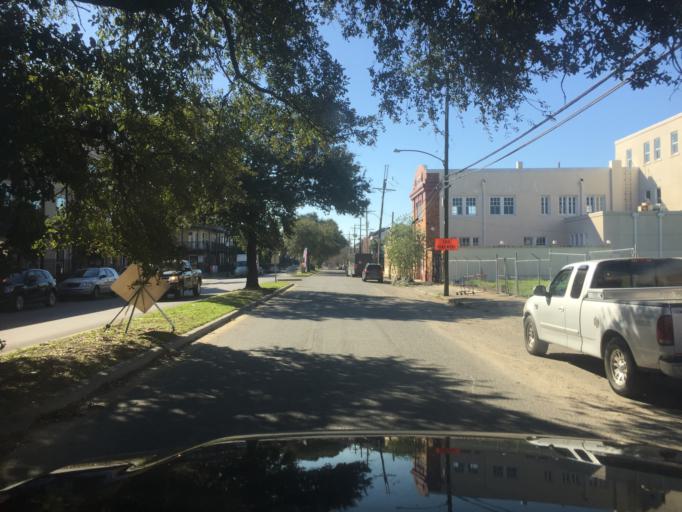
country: US
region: Louisiana
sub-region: Orleans Parish
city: New Orleans
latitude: 29.9364
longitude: -90.0692
